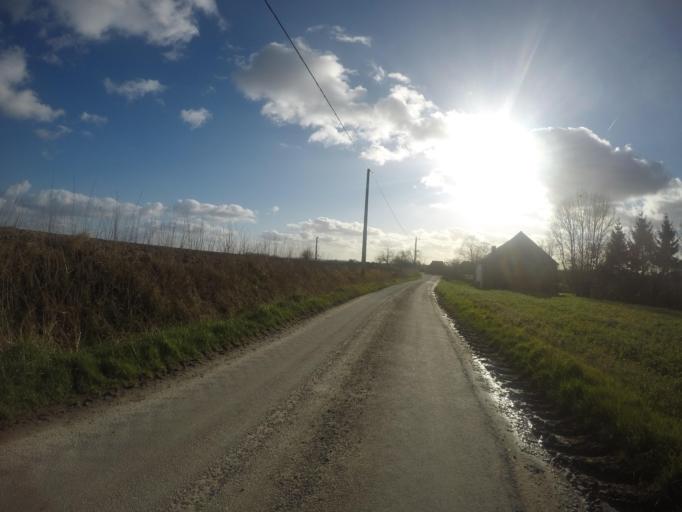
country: BE
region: Wallonia
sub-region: Province du Hainaut
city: Enghien
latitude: 50.6474
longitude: 4.0511
